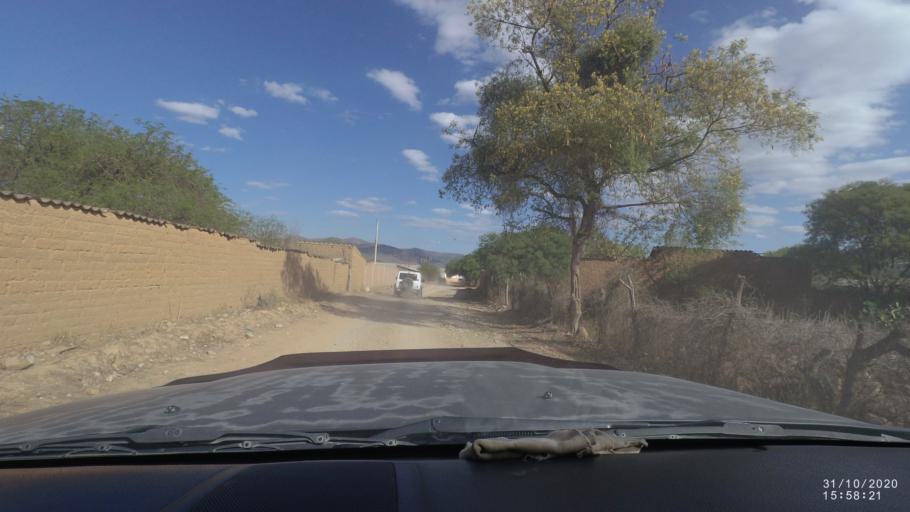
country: BO
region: Chuquisaca
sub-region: Provincia Zudanez
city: Mojocoya
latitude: -18.3251
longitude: -64.6722
